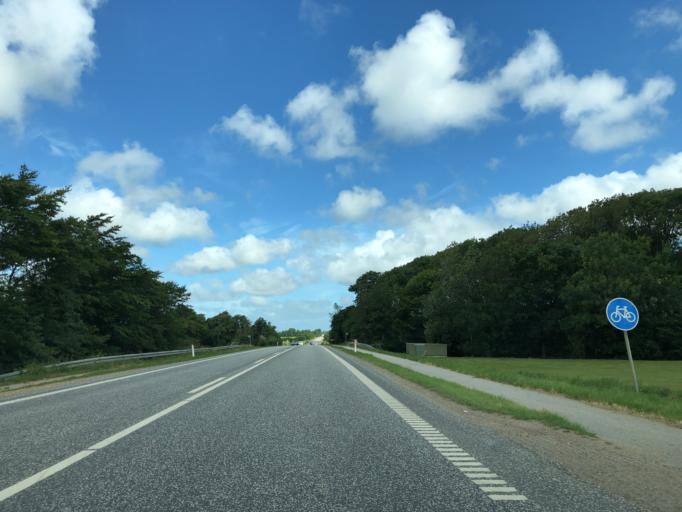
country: DK
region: Central Jutland
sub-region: Struer Kommune
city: Struer
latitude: 56.4274
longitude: 8.5990
